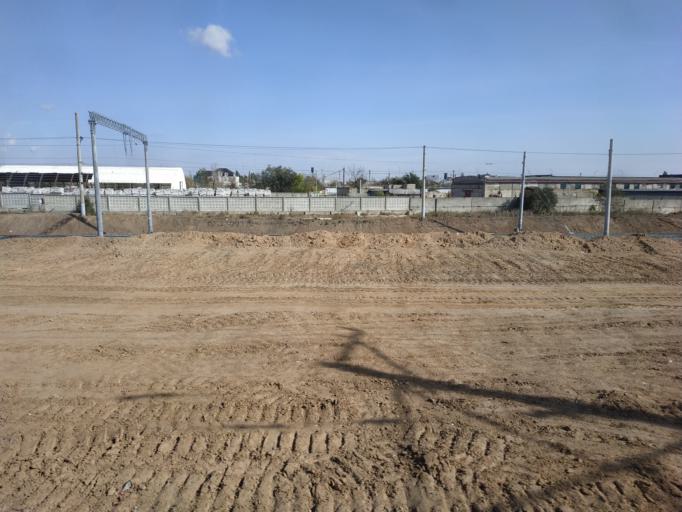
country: RU
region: Volgograd
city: Gumrak
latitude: 48.7726
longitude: 44.3850
